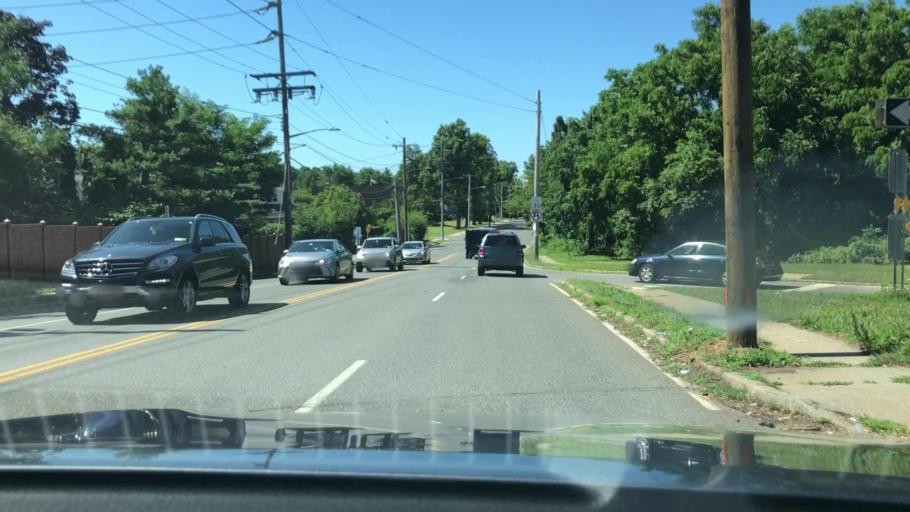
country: US
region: New York
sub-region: Nassau County
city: North Valley Stream
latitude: 40.6824
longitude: -73.6888
